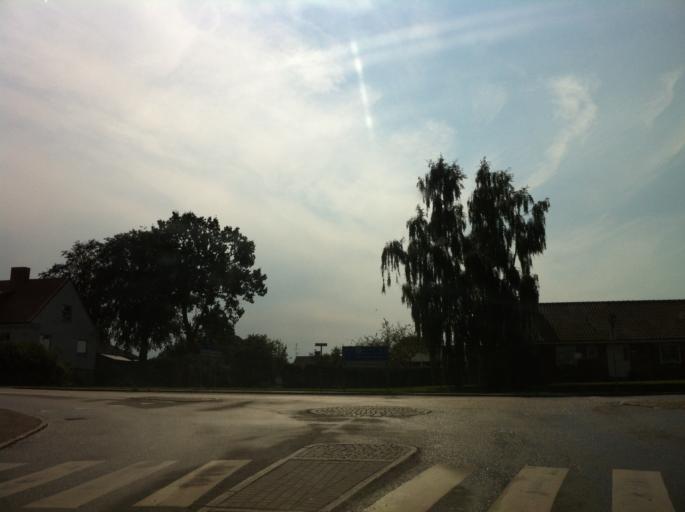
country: SE
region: Skane
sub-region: Helsingborg
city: Glumslov
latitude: 55.9649
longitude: 12.8657
